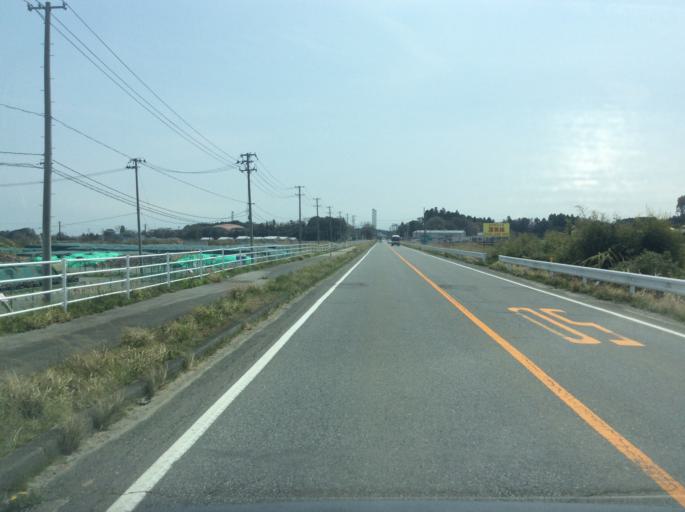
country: JP
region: Fukushima
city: Namie
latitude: 37.2717
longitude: 140.9933
